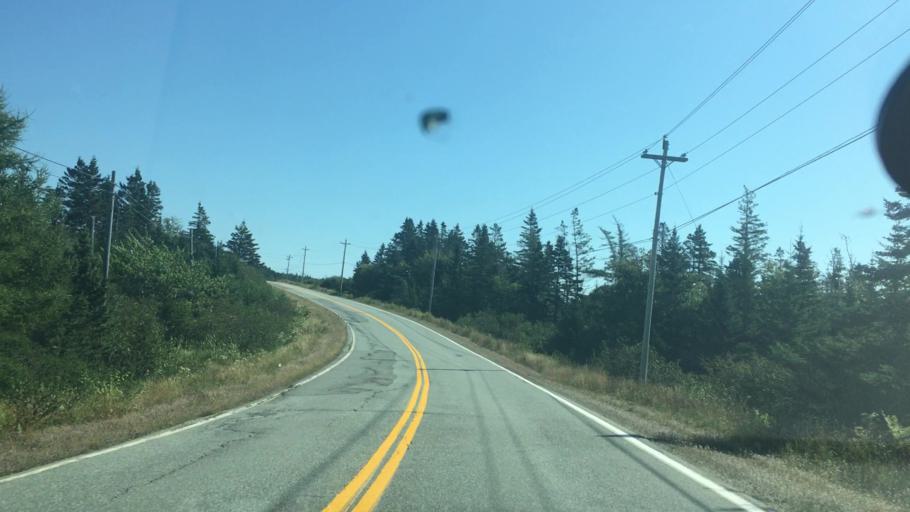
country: CA
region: Nova Scotia
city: New Glasgow
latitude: 44.9171
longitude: -62.3276
